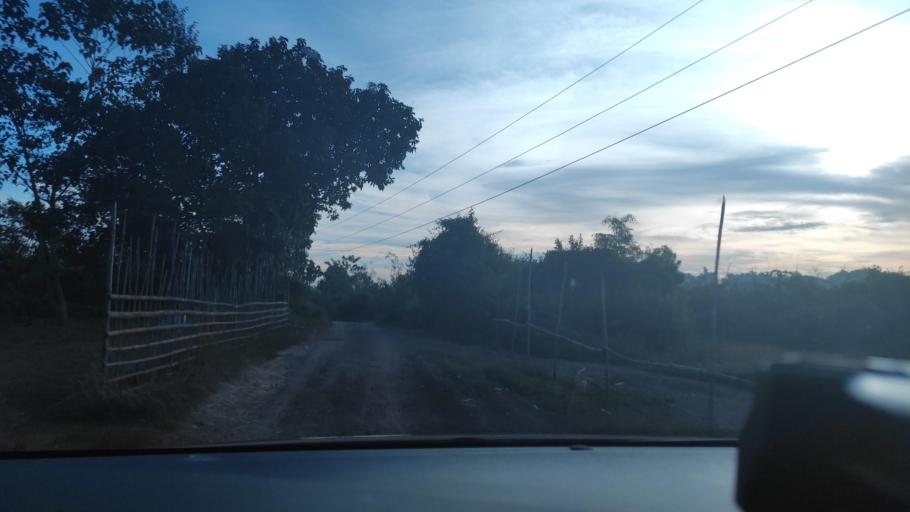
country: PH
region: Ilocos
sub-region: Province of Pangasinan
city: Balingasay
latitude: 16.3065
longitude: 119.8608
